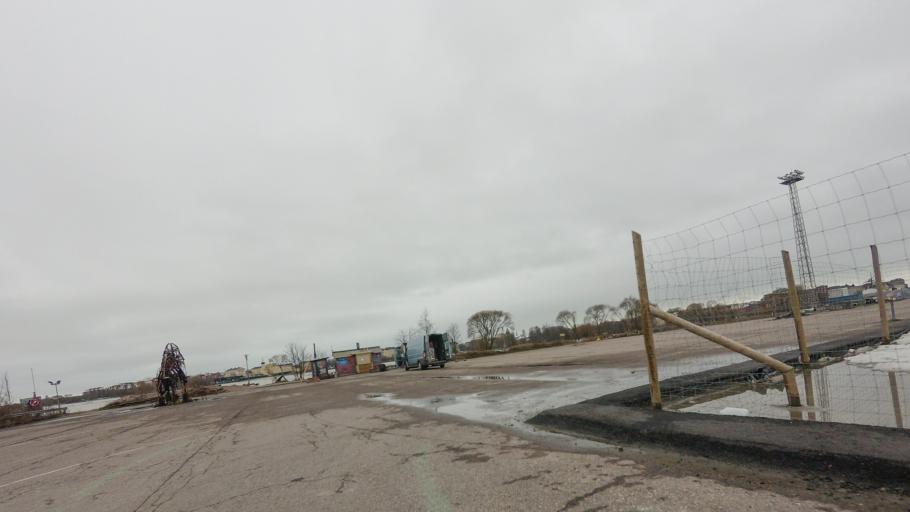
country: FI
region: Uusimaa
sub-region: Helsinki
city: Helsinki
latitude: 60.1781
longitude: 24.9727
